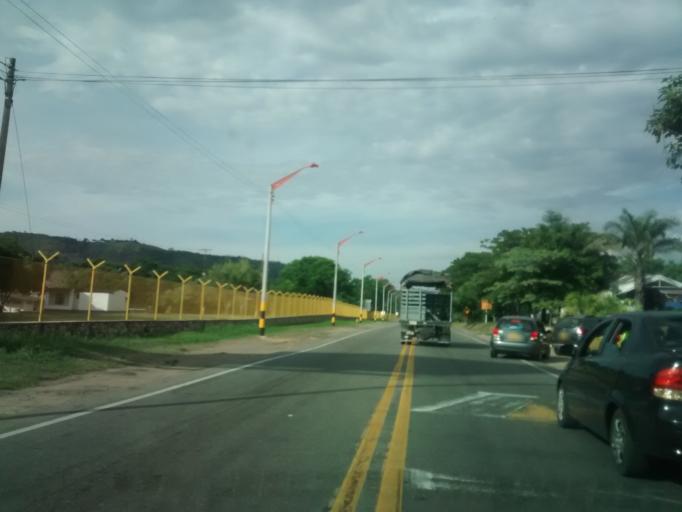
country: CO
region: Tolima
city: Melgar
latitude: 4.2200
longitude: -74.6267
